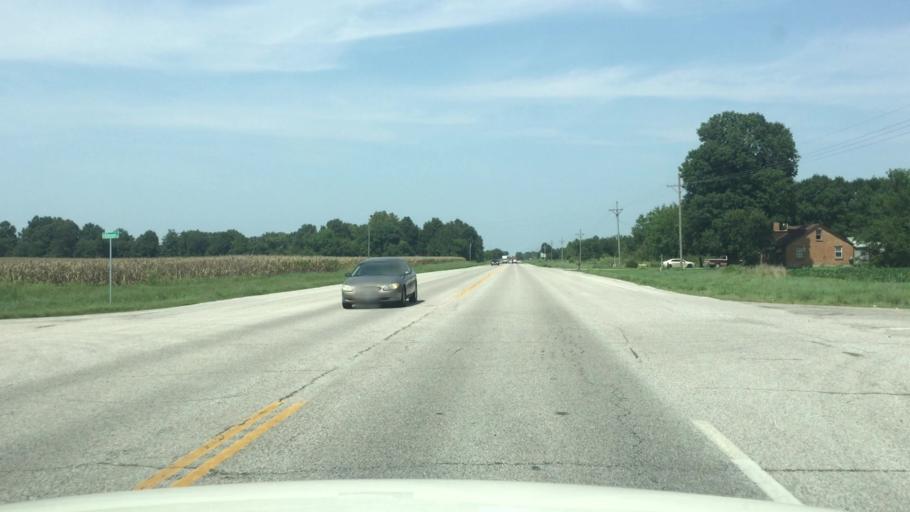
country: US
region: Kansas
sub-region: Cherokee County
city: Galena
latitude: 37.1485
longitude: -94.7042
